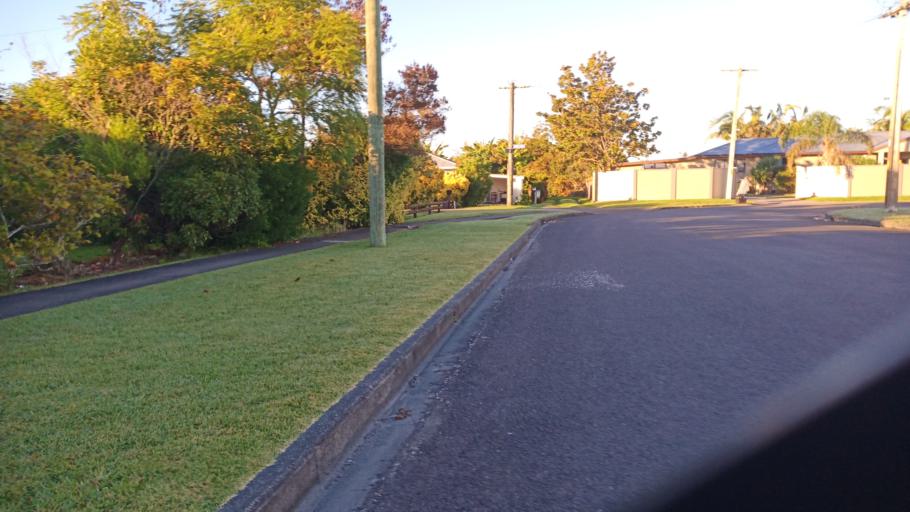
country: NZ
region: Gisborne
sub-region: Gisborne District
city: Gisborne
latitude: -38.6522
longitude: 177.9927
